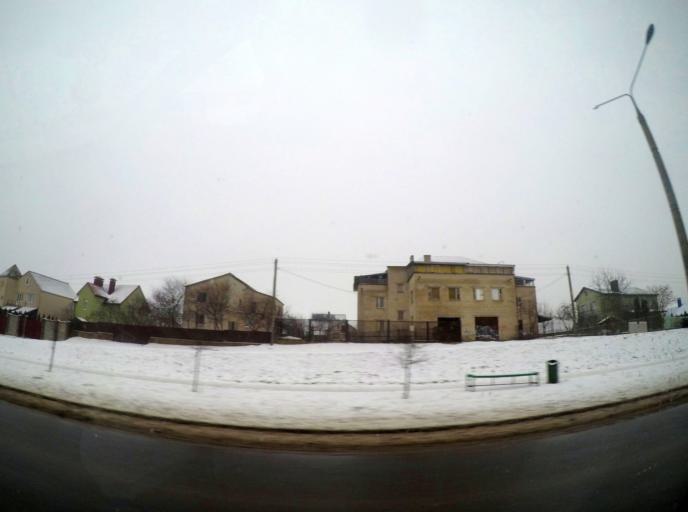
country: BY
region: Grodnenskaya
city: Hrodna
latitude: 53.6292
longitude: 23.8047
